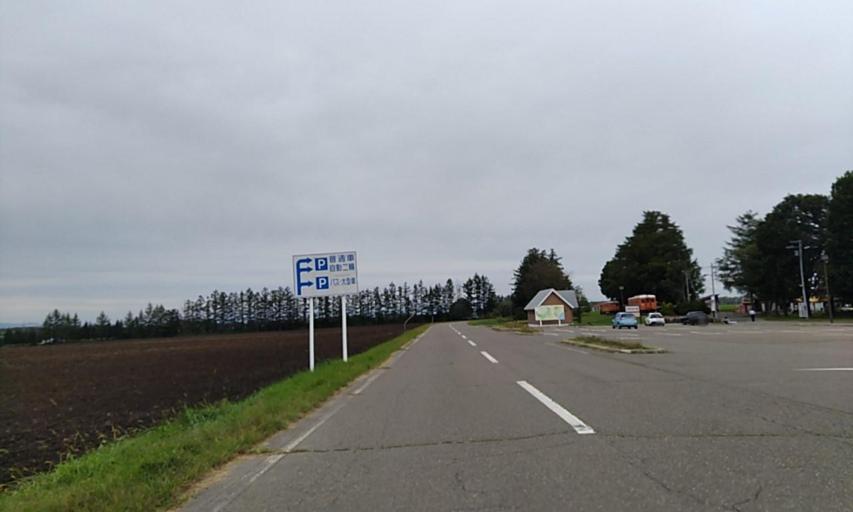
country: JP
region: Hokkaido
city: Obihiro
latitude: 42.7439
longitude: 143.1613
